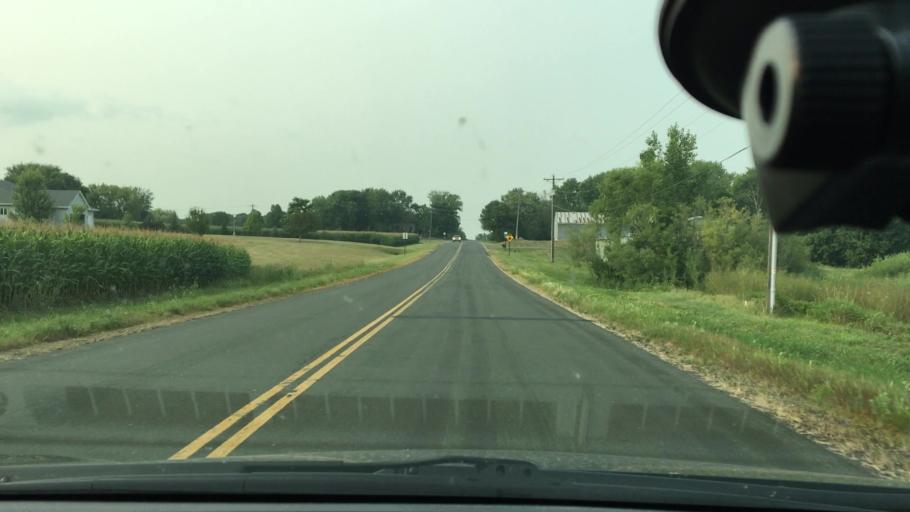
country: US
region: Minnesota
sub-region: Wright County
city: Albertville
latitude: 45.2878
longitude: -93.6839
